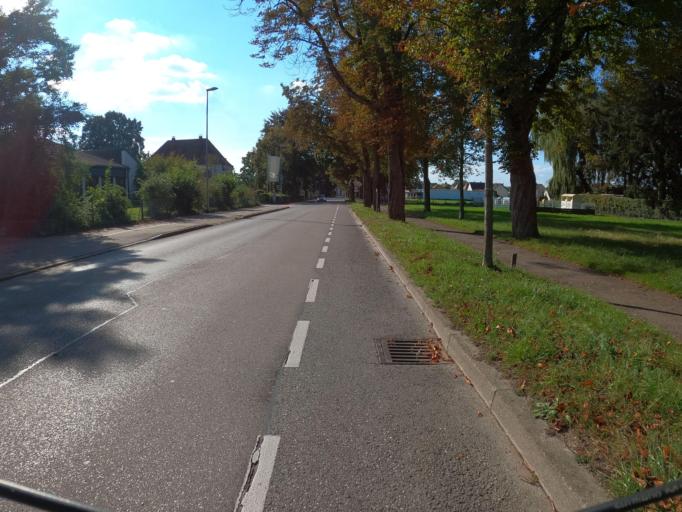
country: DE
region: Bavaria
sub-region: Swabia
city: Weissenhorn
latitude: 48.3041
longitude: 10.1679
